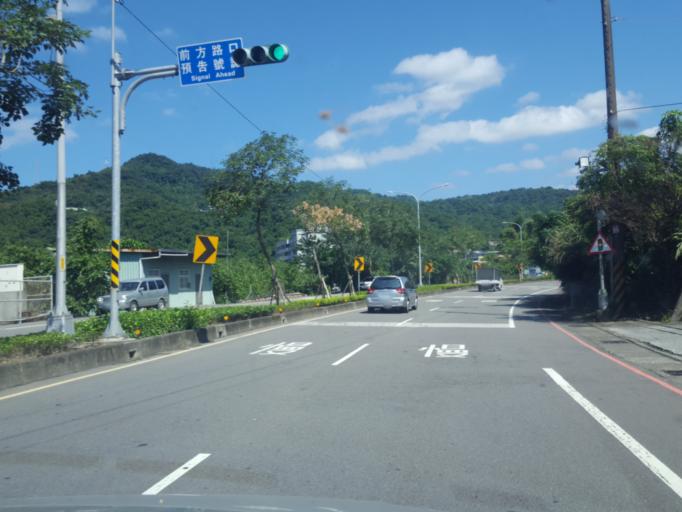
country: TW
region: Taipei
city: Taipei
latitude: 25.0073
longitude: 121.6321
